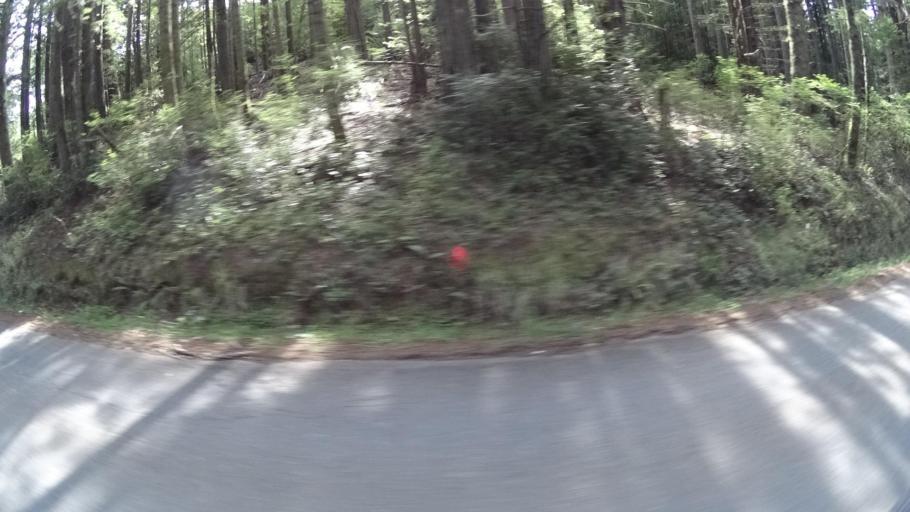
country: US
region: California
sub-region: Humboldt County
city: Bayside
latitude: 40.7577
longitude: -124.0018
